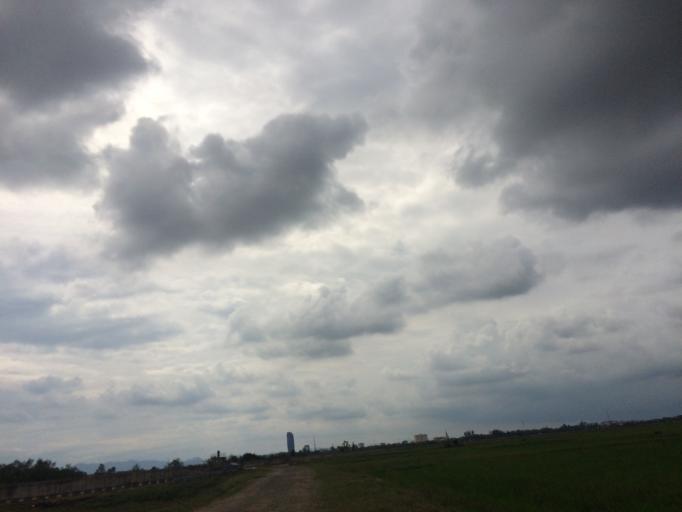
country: VN
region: Ha Tinh
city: Ha Tinh
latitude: 18.3379
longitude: 105.9300
